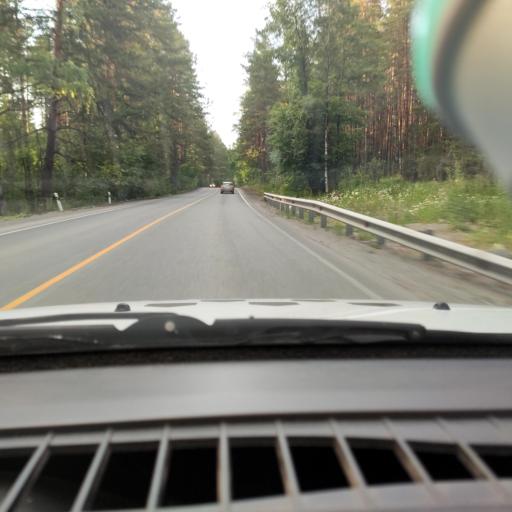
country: RU
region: Chelyabinsk
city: Turgoyak
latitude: 55.2575
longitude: 60.1979
